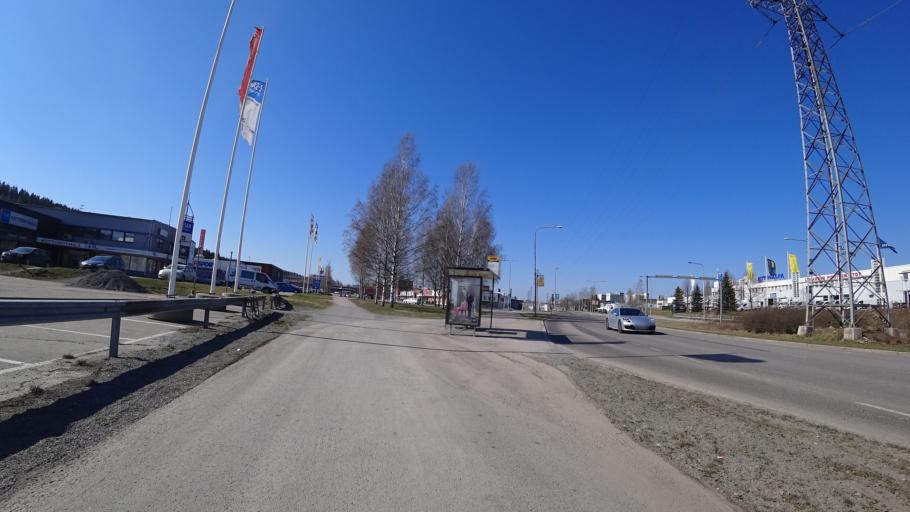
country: FI
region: Pirkanmaa
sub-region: Tampere
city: Pirkkala
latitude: 61.5138
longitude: 23.6736
